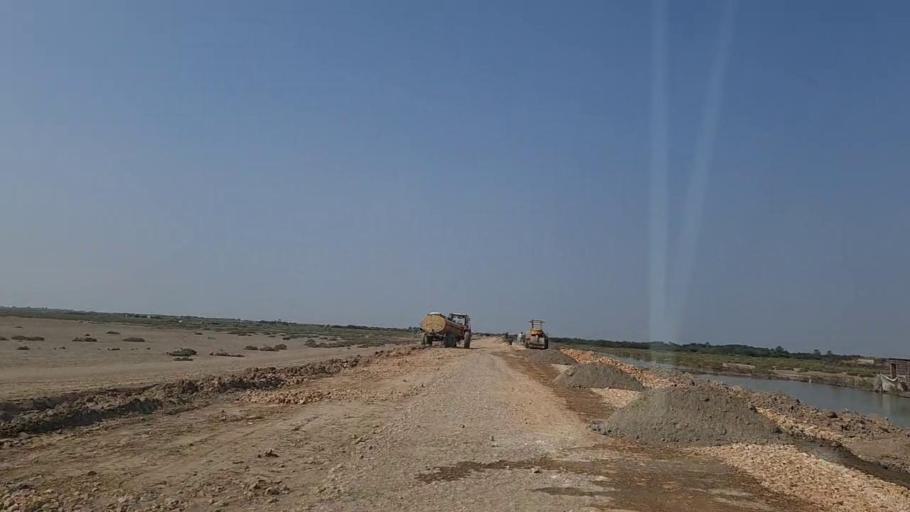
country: PK
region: Sindh
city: Chuhar Jamali
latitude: 24.1921
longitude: 67.8411
